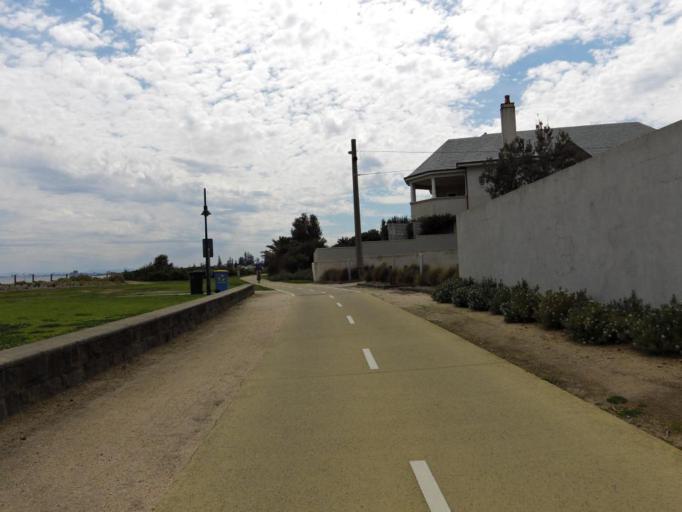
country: AU
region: Victoria
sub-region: Port Phillip
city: Elwood
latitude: -37.8955
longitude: 144.9864
